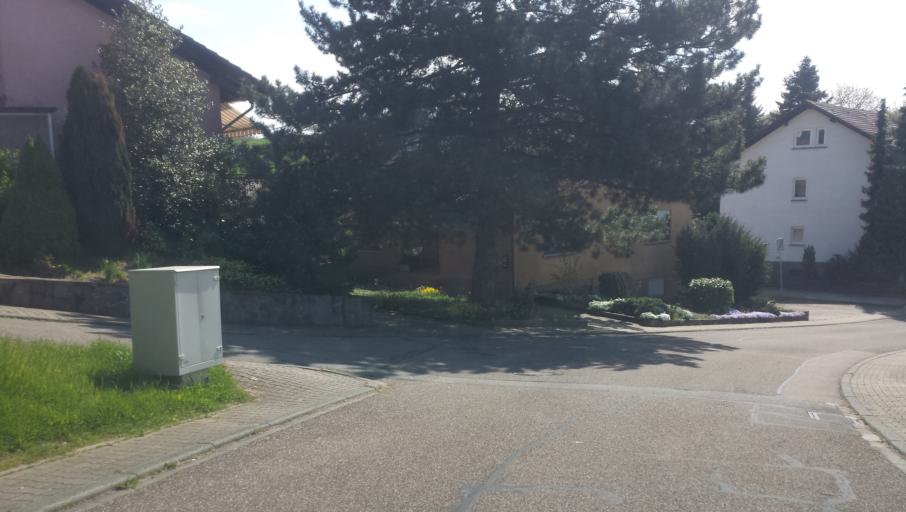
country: DE
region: Baden-Wuerttemberg
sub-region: Karlsruhe Region
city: Horrenberg
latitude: 49.2836
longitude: 8.7865
